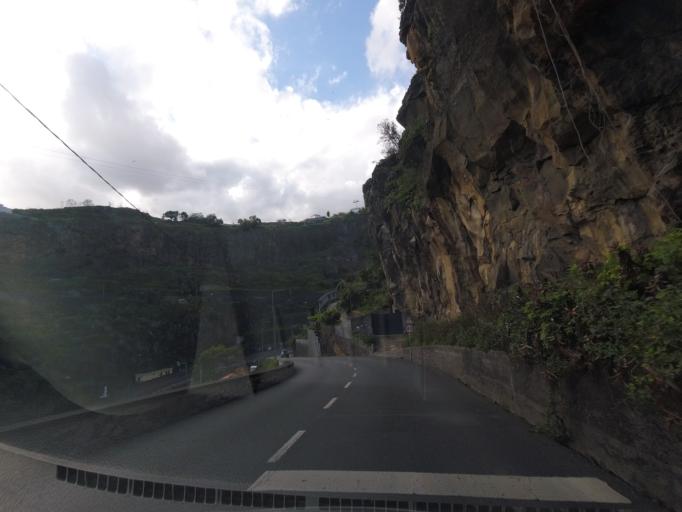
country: PT
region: Madeira
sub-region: Funchal
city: Nossa Senhora do Monte
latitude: 32.6595
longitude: -16.8994
